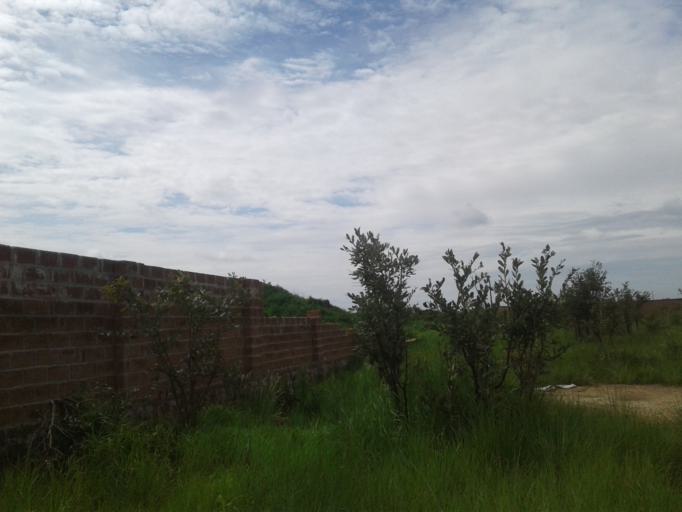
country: CD
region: Katanga
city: Lubumbashi
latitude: -11.4666
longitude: 27.5467
